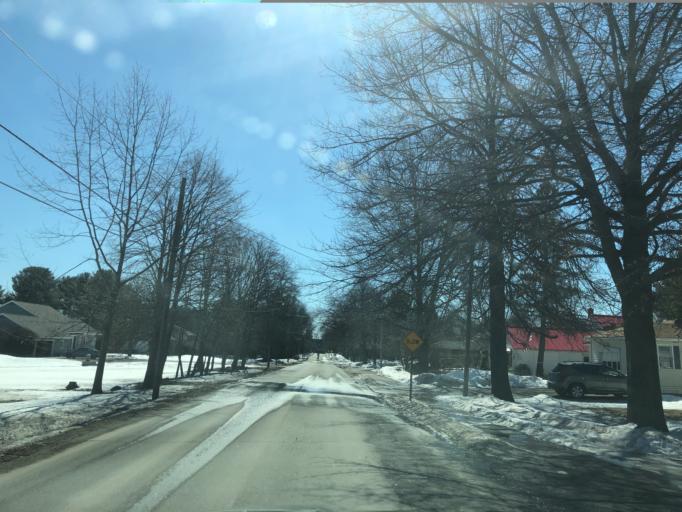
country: US
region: Maine
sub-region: Penobscot County
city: Brewer
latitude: 44.8158
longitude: -68.7538
